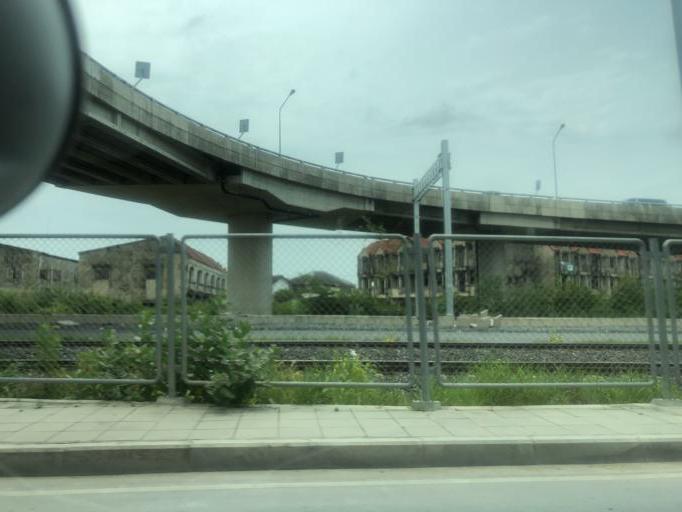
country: TH
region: Bangkok
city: Don Mueang
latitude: 13.9473
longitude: 100.6073
